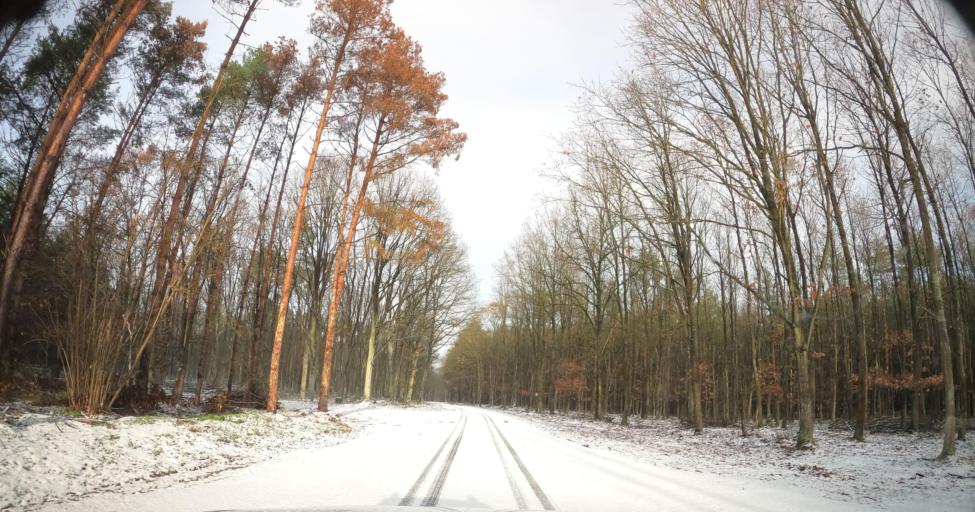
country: PL
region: West Pomeranian Voivodeship
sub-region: Powiat gryfinski
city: Mieszkowice
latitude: 52.7328
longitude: 14.4901
